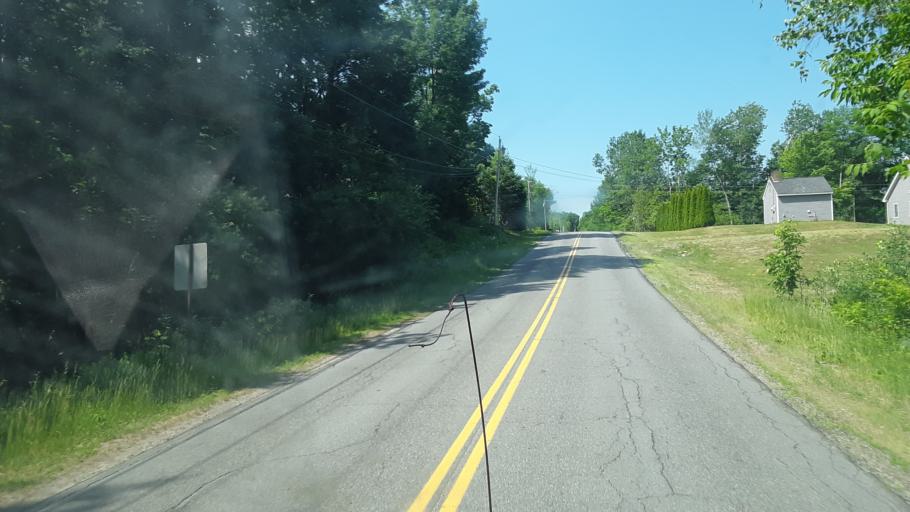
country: US
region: Maine
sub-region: Waldo County
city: Swanville
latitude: 44.5450
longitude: -68.9757
